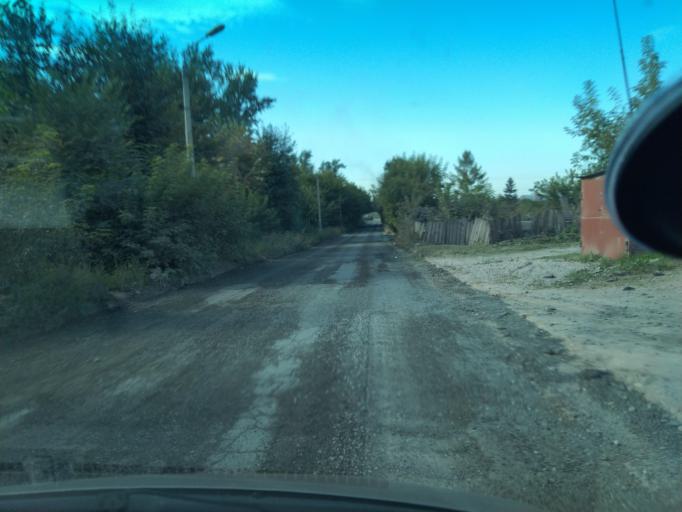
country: RU
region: Krasnoyarskiy
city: Krasnoyarsk
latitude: 55.9736
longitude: 92.9450
